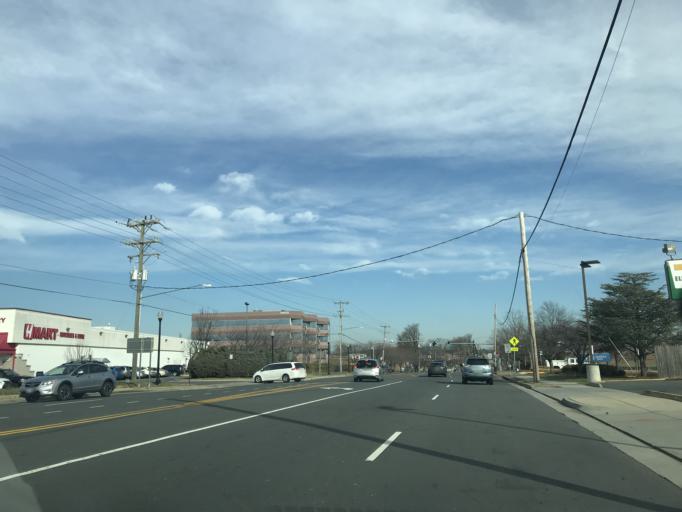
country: US
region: Virginia
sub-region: City of Fairfax
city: Fairfax
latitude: 38.8567
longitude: -77.3317
